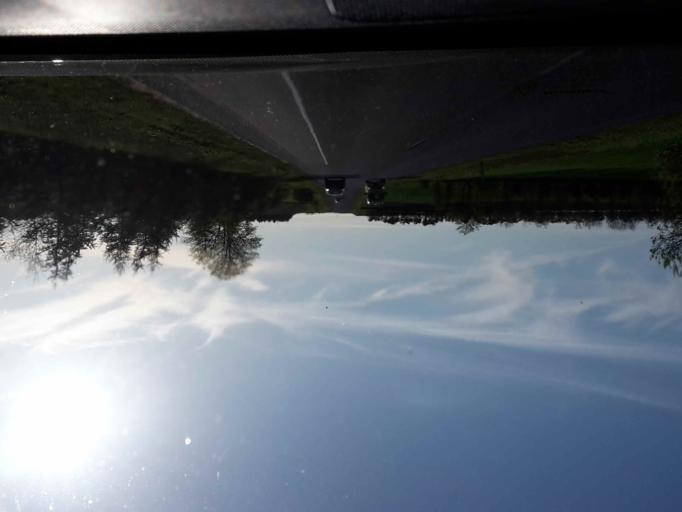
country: DK
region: Central Jutland
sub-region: Randers Kommune
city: Assentoft
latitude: 56.4429
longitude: 10.2237
